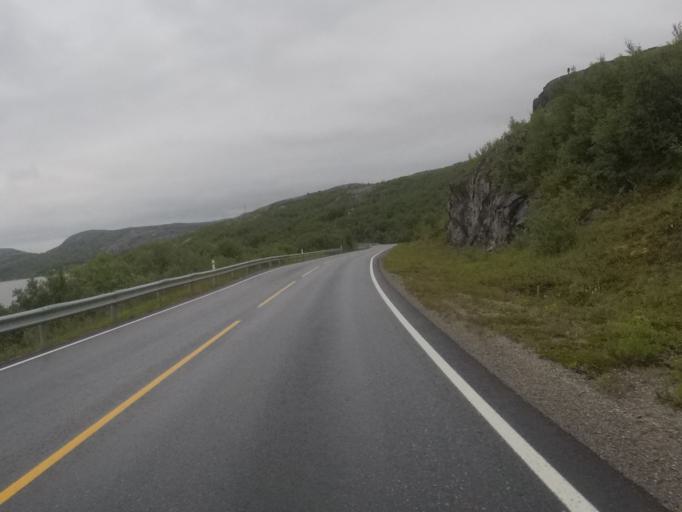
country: NO
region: Finnmark Fylke
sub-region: Sor-Varanger
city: Bjornevatn
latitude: 69.7029
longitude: 29.6146
